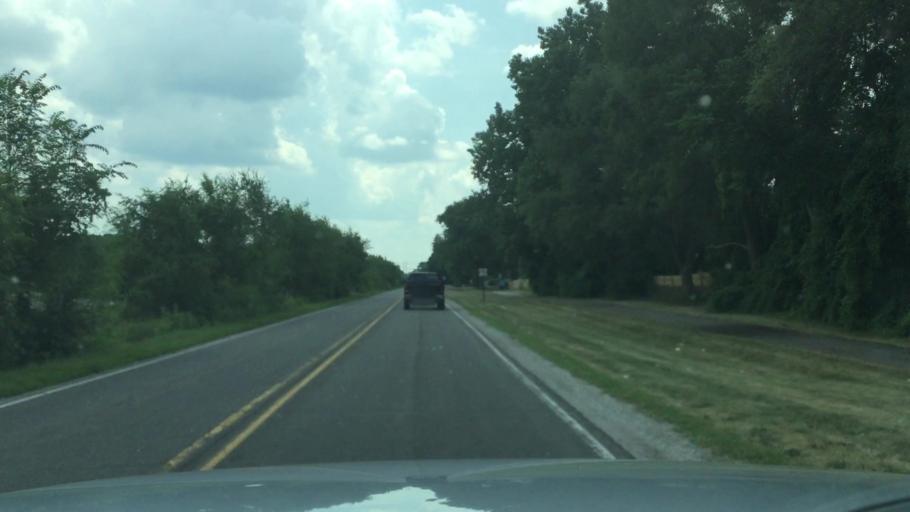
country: US
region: Michigan
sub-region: Washtenaw County
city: Ypsilanti
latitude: 42.2288
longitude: -83.5631
